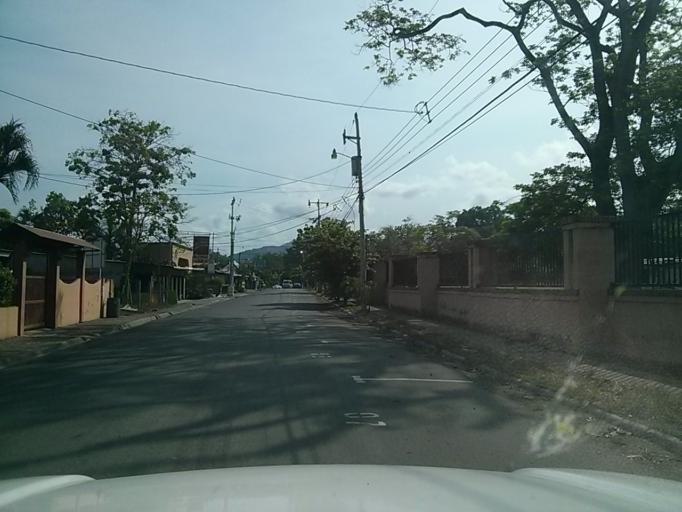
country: CR
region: Puntarenas
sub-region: Canton de Garabito
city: Jaco
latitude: 9.6204
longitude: -84.6377
